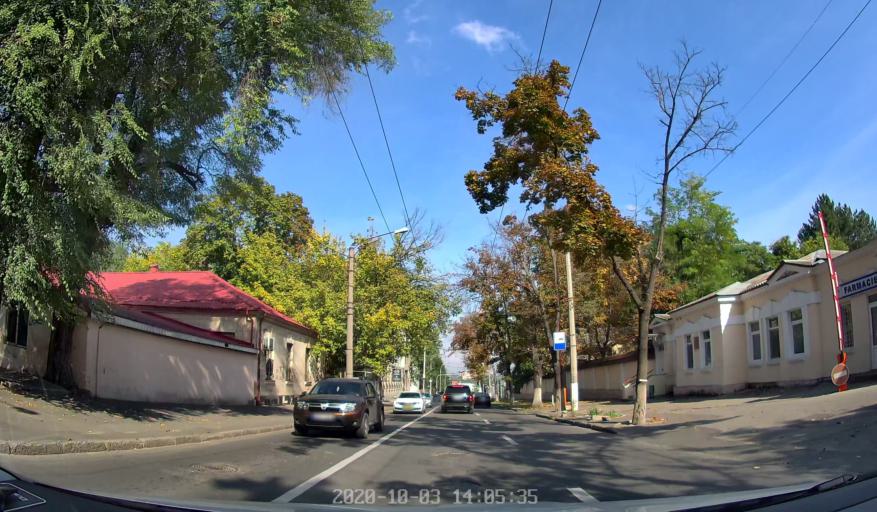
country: MD
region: Chisinau
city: Chisinau
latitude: 47.0331
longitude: 28.8174
